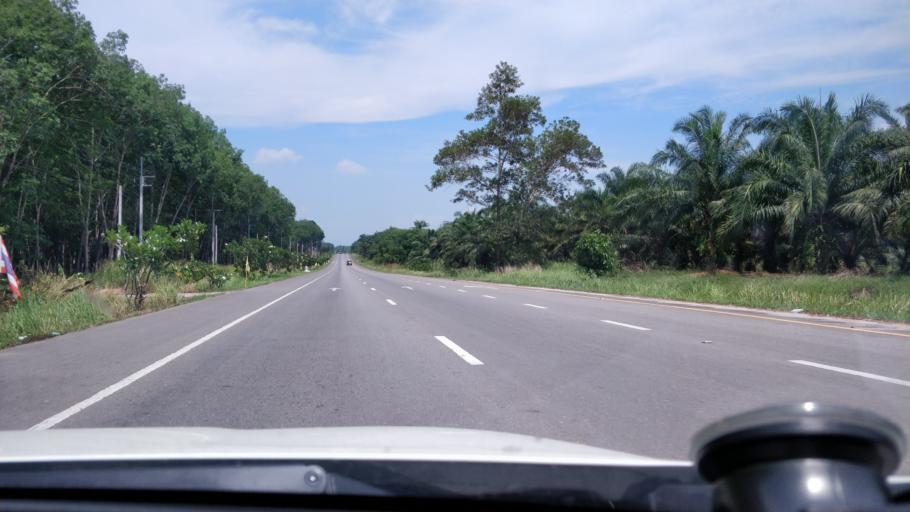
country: TH
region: Surat Thani
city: Chai Buri
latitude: 8.6416
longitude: 99.0676
